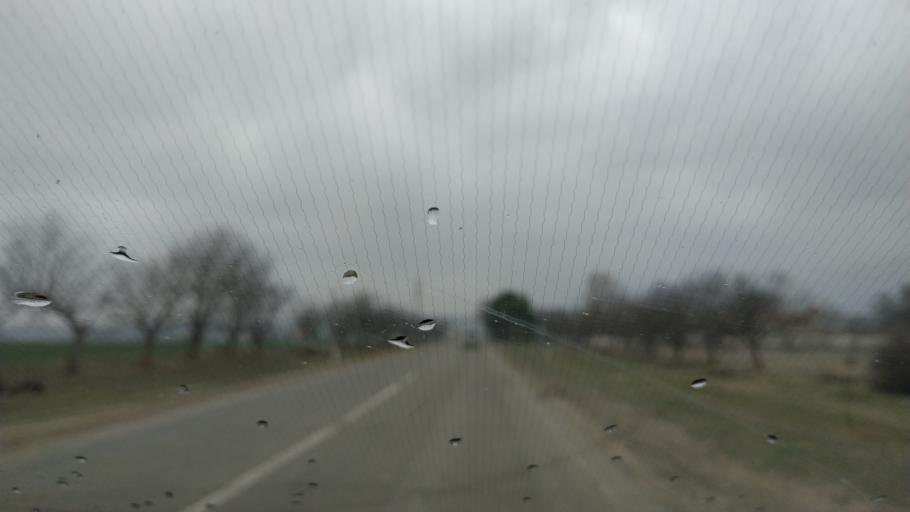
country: MD
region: Gagauzia
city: Comrat
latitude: 46.2473
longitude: 28.7612
